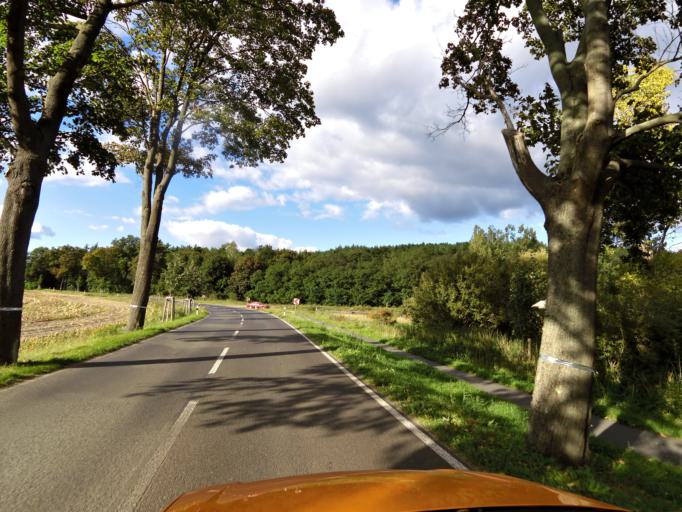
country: DE
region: Brandenburg
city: Trebbin
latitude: 52.1851
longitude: 13.1712
